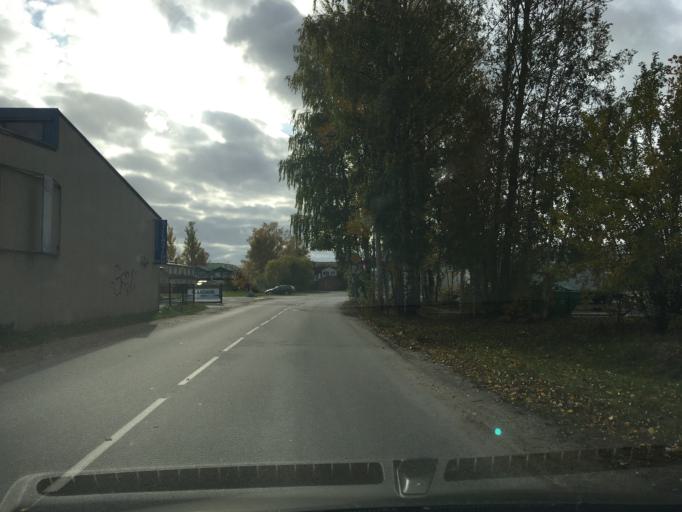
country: EE
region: Paernumaa
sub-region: Paernu linn
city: Parnu
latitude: 58.3737
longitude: 24.5464
